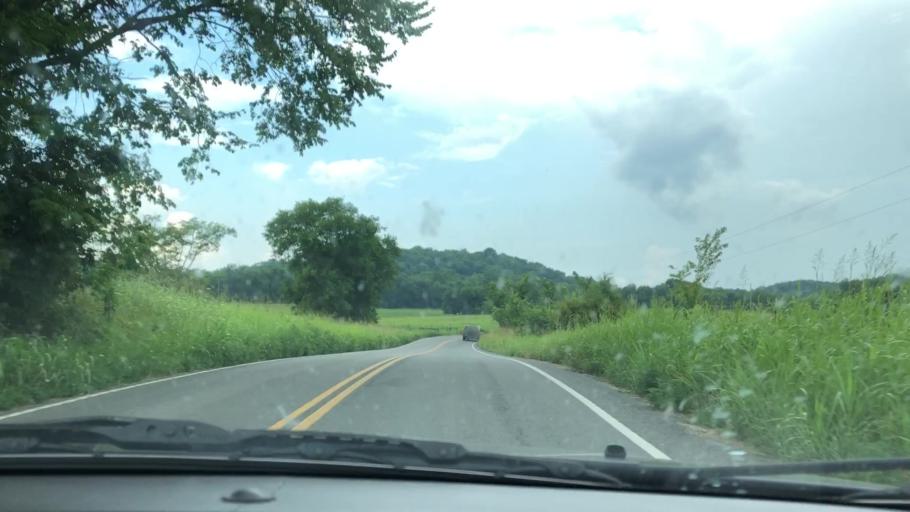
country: US
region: Tennessee
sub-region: Maury County
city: Spring Hill
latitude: 35.7823
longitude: -87.0040
